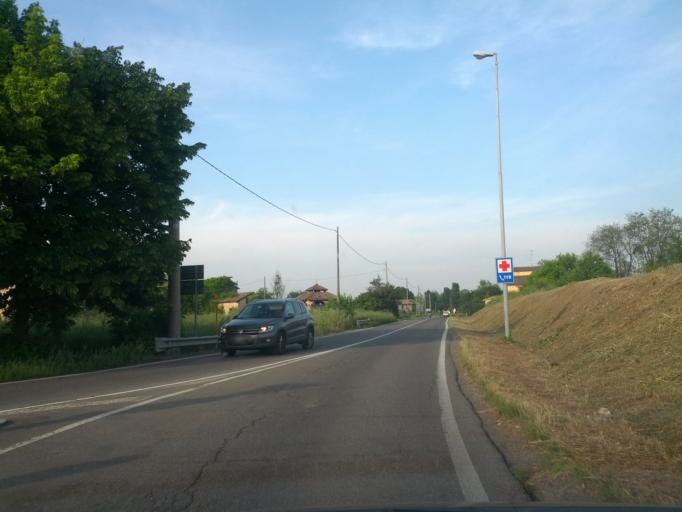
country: IT
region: Emilia-Romagna
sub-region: Provincia di Reggio Emilia
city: Bagnolo in Piano
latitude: 44.7651
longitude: 10.6804
